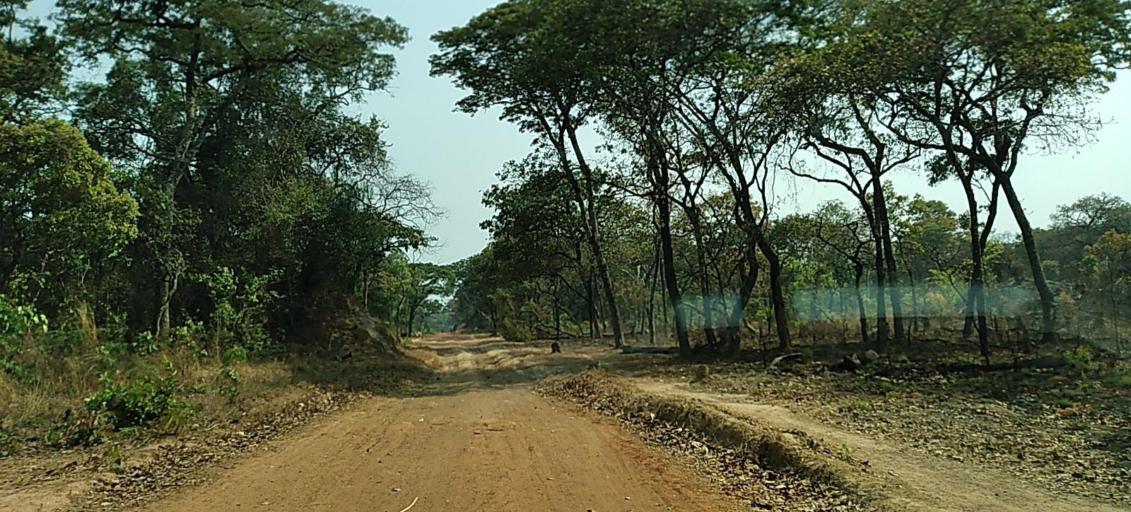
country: ZM
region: North-Western
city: Kansanshi
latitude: -12.0723
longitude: 26.8880
